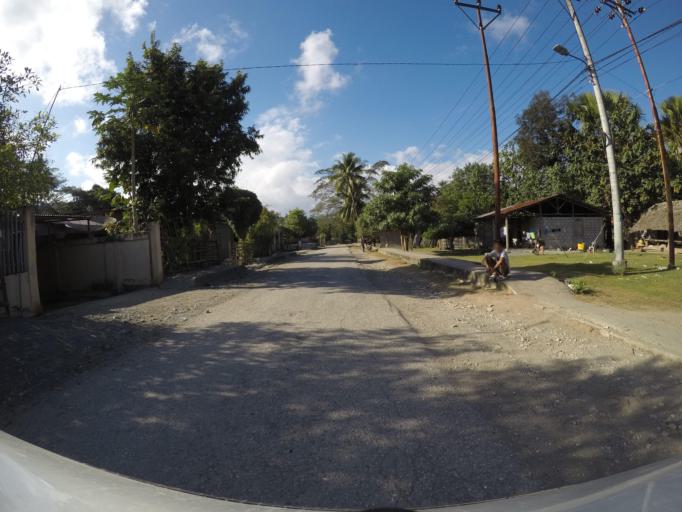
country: TL
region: Viqueque
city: Viqueque
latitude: -8.8538
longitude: 126.3659
